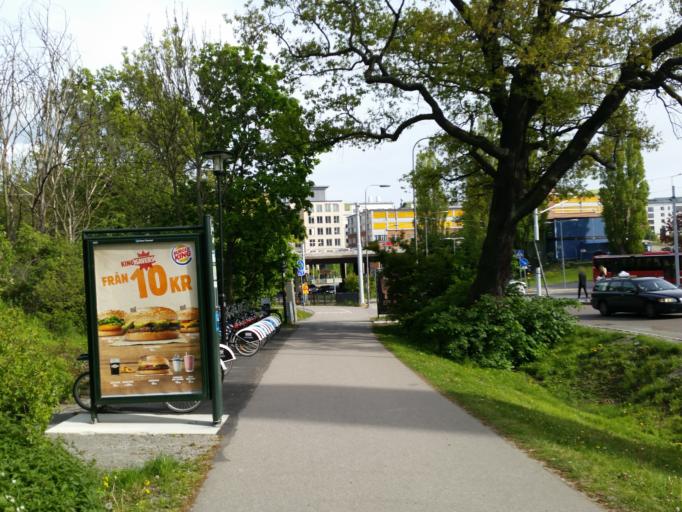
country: SE
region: Stockholm
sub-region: Stockholms Kommun
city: Arsta
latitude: 59.3108
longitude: 18.0250
